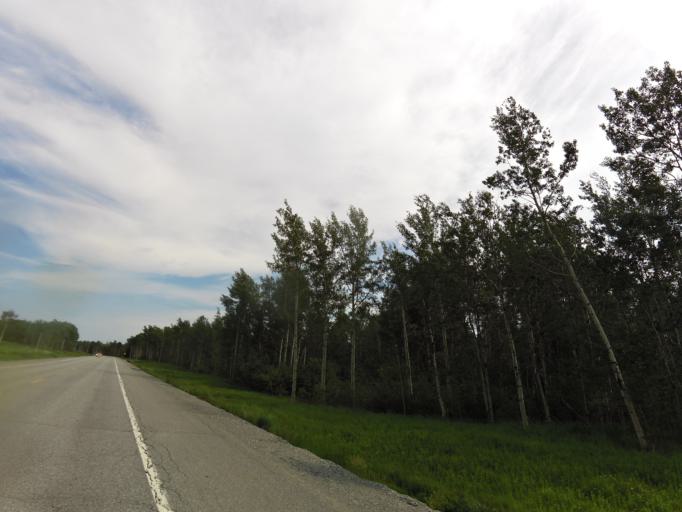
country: CA
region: Quebec
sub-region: Abitibi-Temiscamingue
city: Malartic
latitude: 48.2298
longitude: -78.4046
